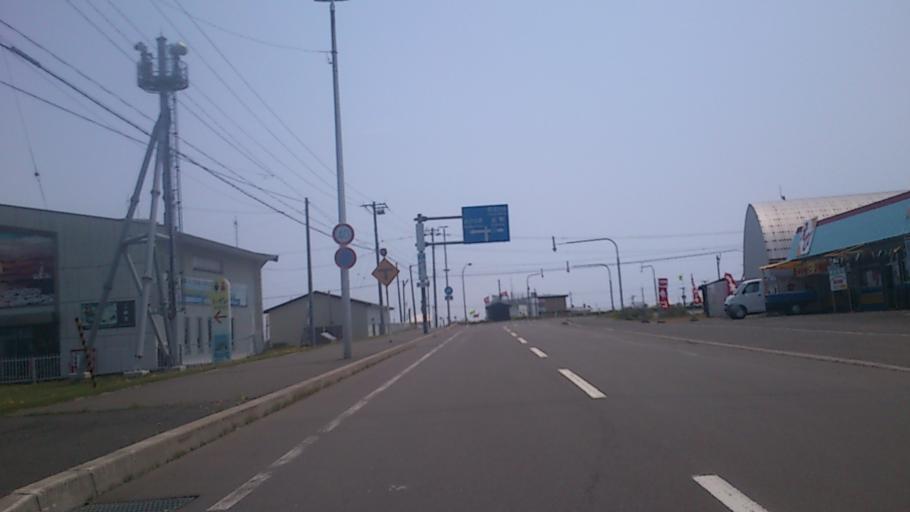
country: JP
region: Hokkaido
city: Nemuro
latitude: 43.3852
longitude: 145.8105
